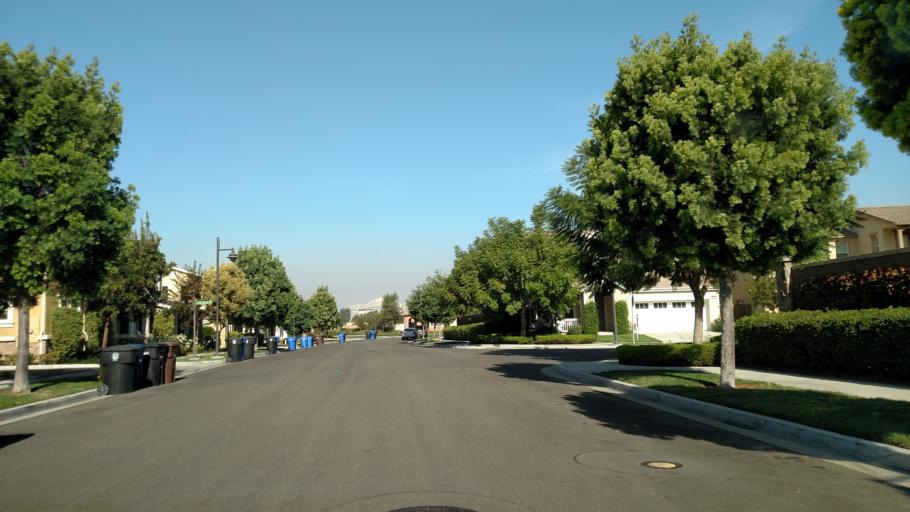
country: US
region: California
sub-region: Orange County
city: Irvine
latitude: 33.6955
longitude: -117.8137
